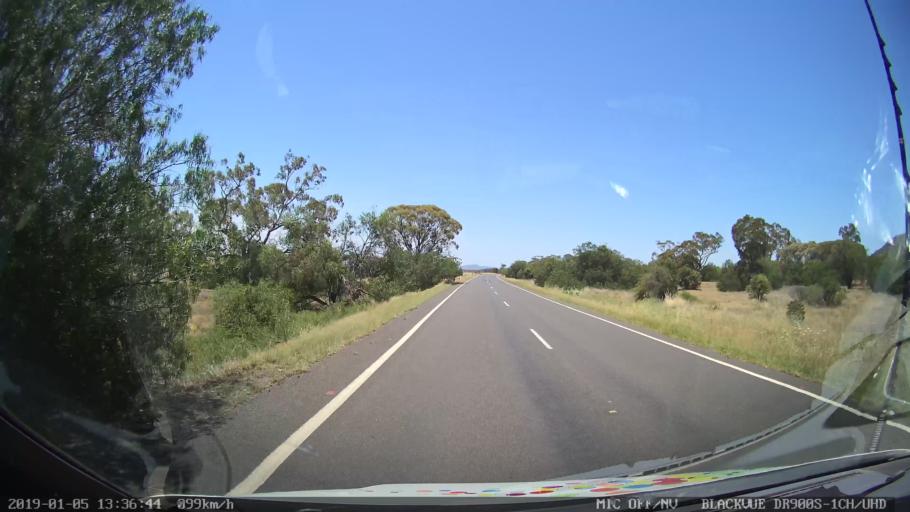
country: AU
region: New South Wales
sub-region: Gunnedah
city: Gunnedah
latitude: -30.9834
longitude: 150.1693
